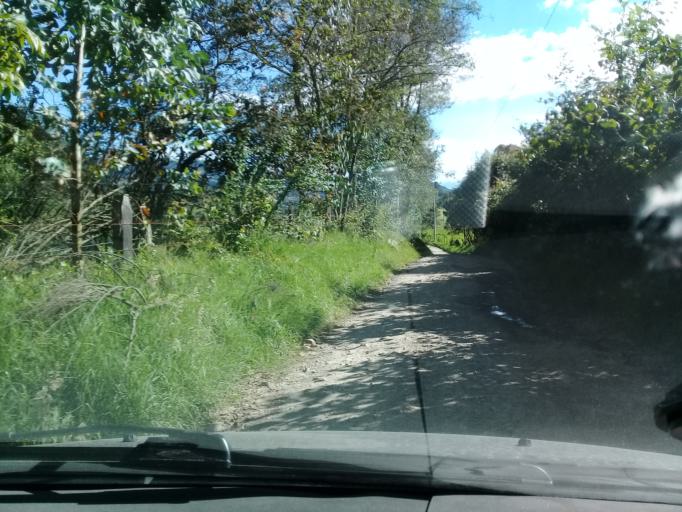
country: CO
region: Cundinamarca
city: Zipaquira
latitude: 5.0082
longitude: -74.0692
